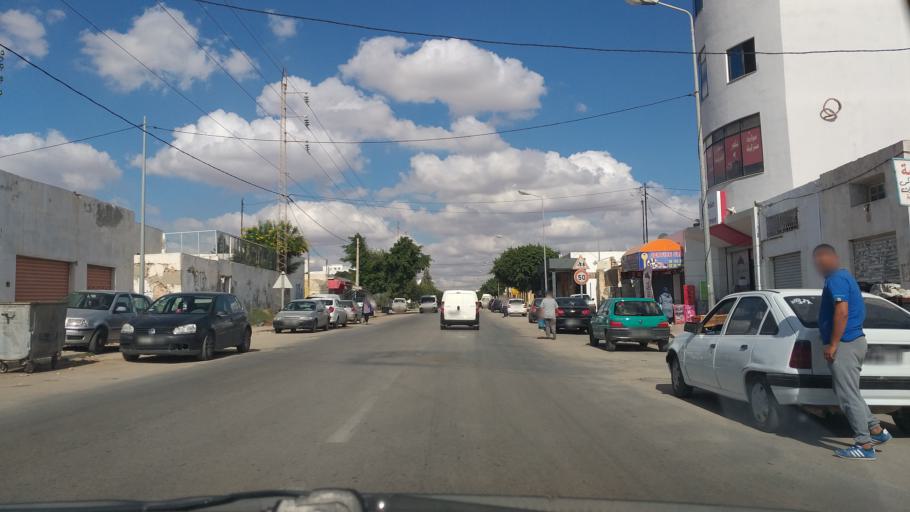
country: TN
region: Safaqis
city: Al Qarmadah
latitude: 34.7705
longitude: 10.7747
